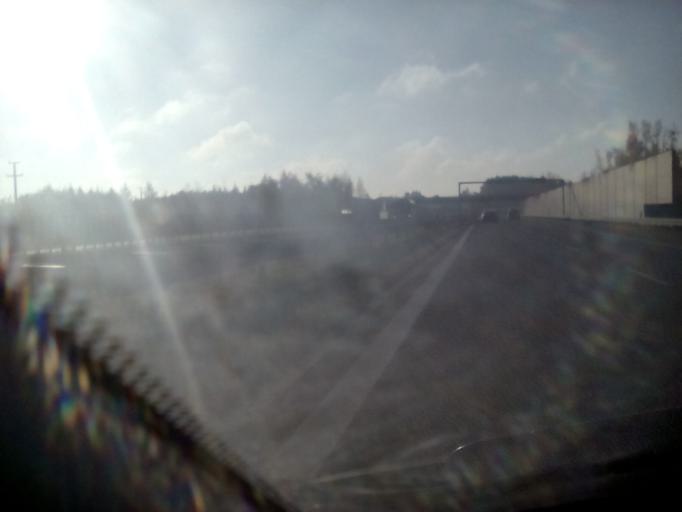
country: PL
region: Masovian Voivodeship
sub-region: Powiat grojecki
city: Grojec
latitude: 51.9023
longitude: 20.8592
